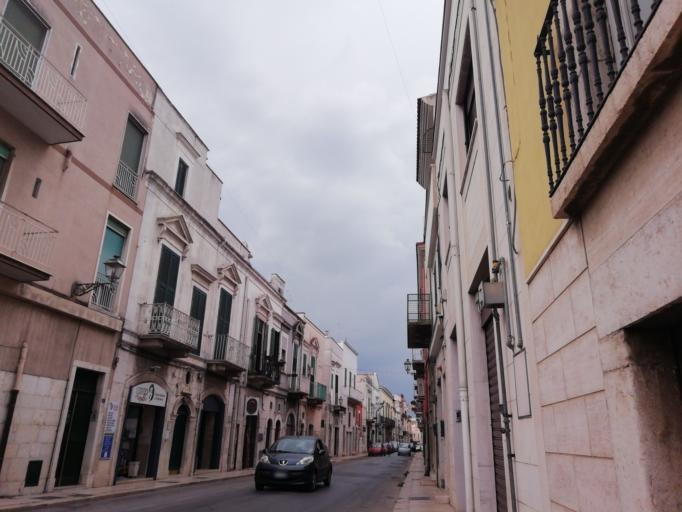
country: IT
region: Apulia
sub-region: Provincia di Barletta - Andria - Trani
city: Andria
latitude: 41.2235
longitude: 16.2954
